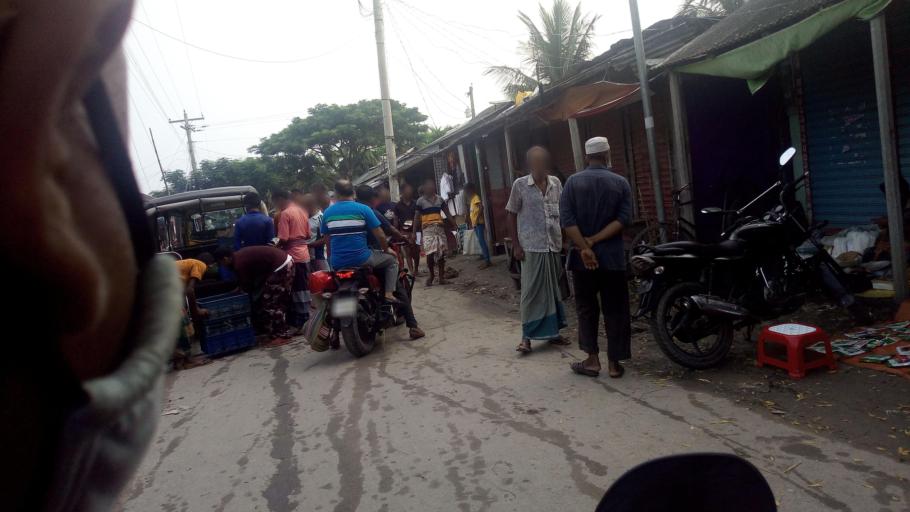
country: BD
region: Khulna
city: Phultala
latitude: 22.6666
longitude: 89.4031
